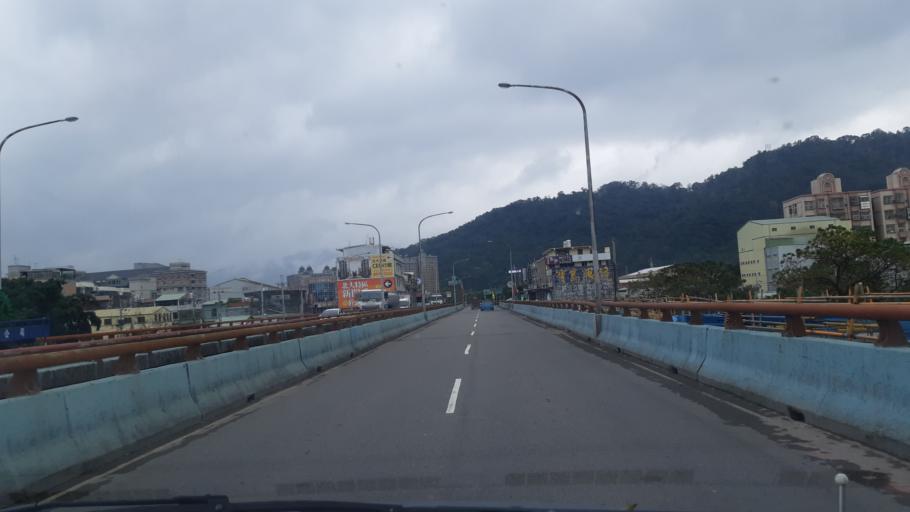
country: TW
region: Taiwan
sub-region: Taoyuan
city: Taoyuan
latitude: 24.9426
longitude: 121.3549
